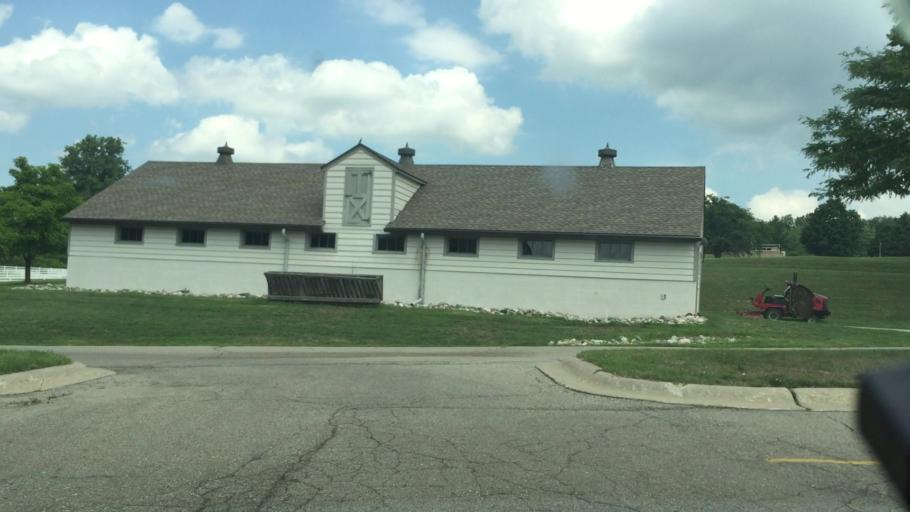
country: US
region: Michigan
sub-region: Oakland County
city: Auburn Hills
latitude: 42.6737
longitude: -83.1995
